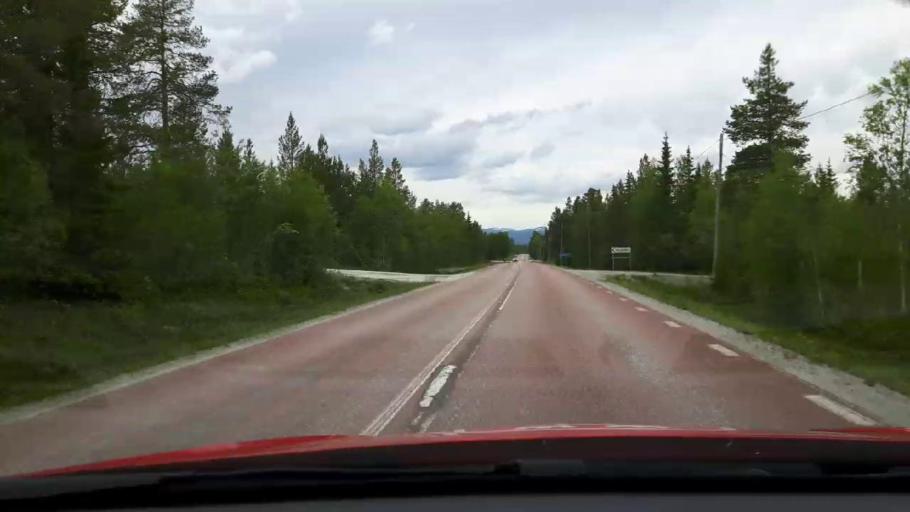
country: NO
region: Hedmark
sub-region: Engerdal
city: Engerdal
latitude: 62.5033
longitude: 12.6228
